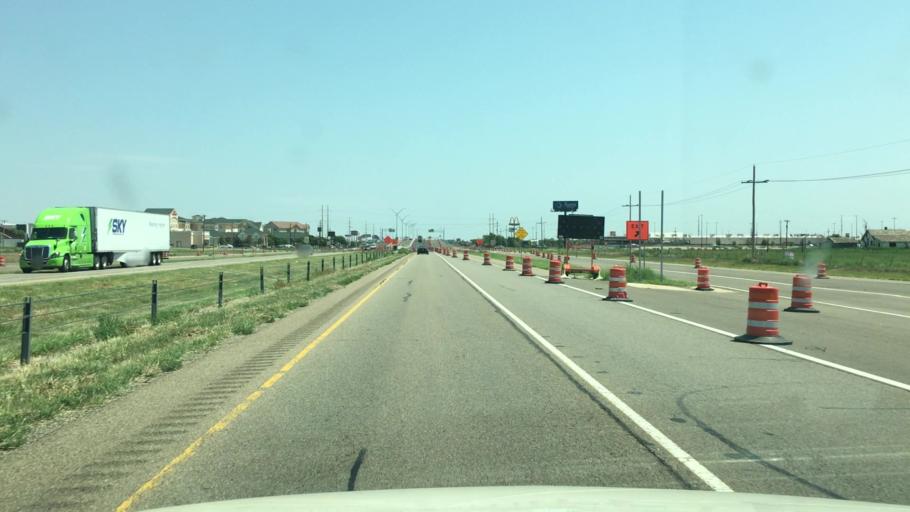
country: US
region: Texas
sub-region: Potter County
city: Bushland
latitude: 35.1872
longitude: -101.9460
